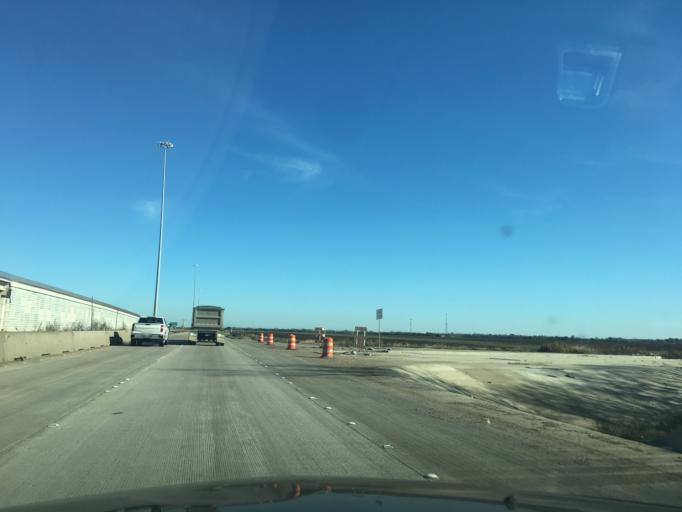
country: US
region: Texas
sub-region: Fort Bend County
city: Rosenberg
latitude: 29.5341
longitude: -95.8464
